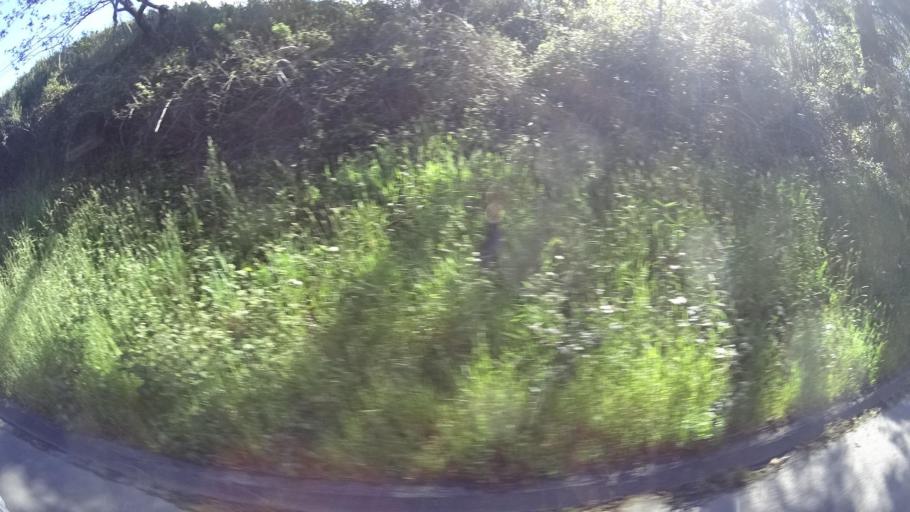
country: US
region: California
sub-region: Humboldt County
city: McKinleyville
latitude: 40.9239
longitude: -124.0998
